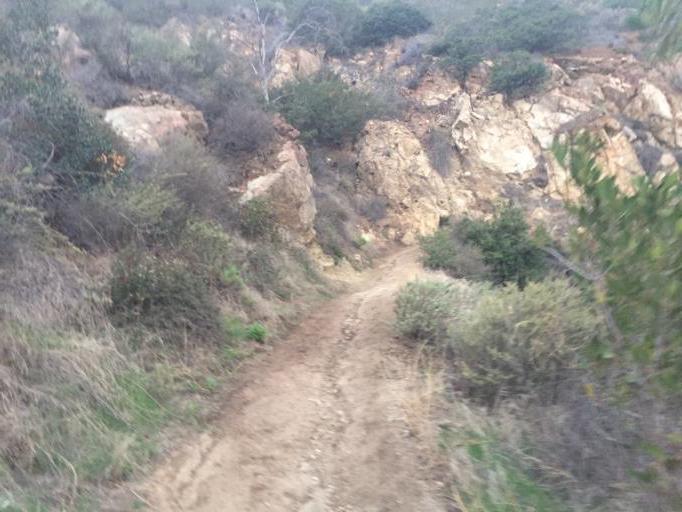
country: US
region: California
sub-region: Los Angeles County
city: Sierra Madre
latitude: 34.1782
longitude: -118.0459
